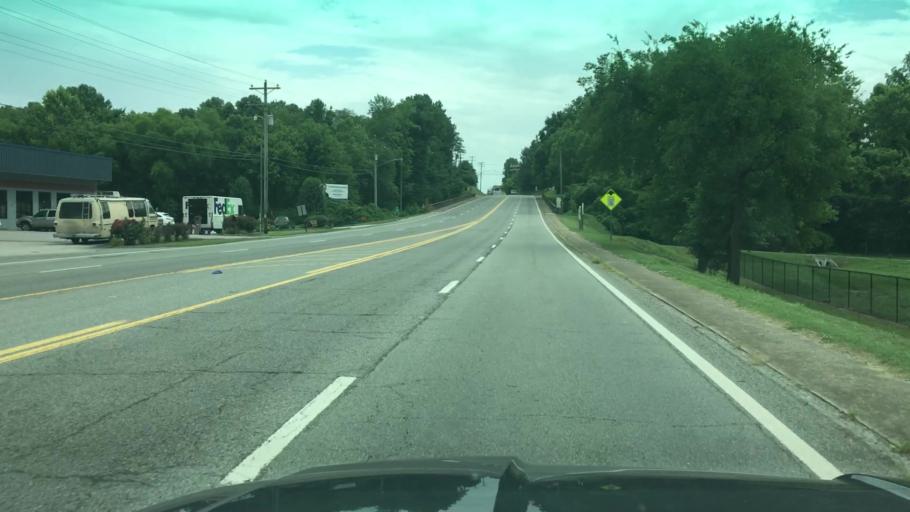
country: US
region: Tennessee
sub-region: Coffee County
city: Manchester
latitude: 35.4816
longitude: -86.0788
